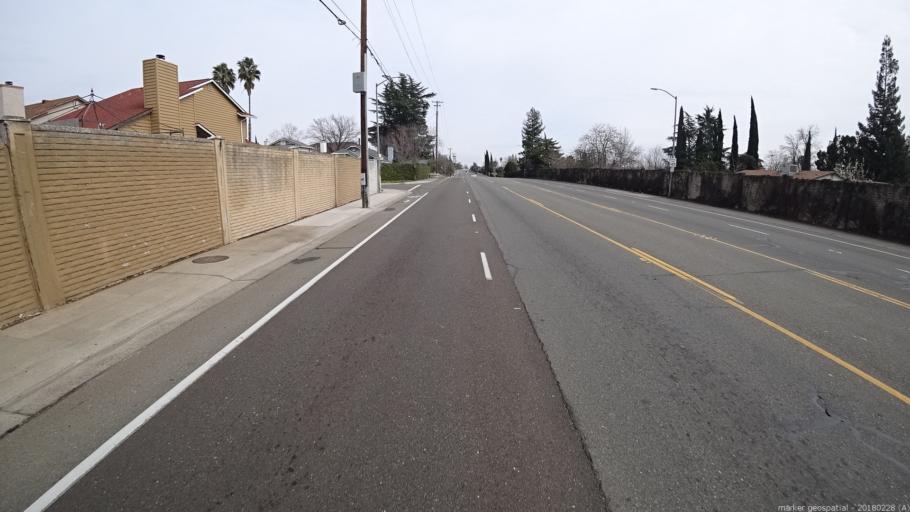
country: US
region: California
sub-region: Sacramento County
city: Antelope
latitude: 38.7038
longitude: -121.3445
